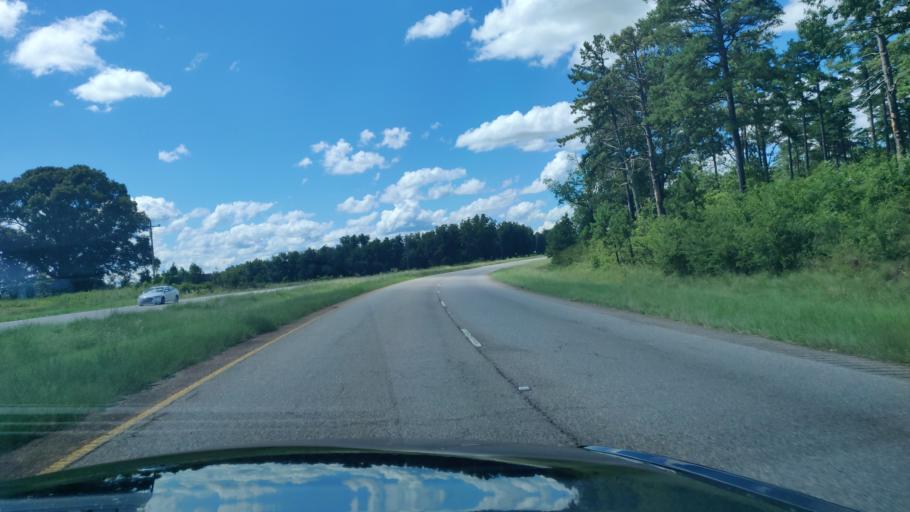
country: US
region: Georgia
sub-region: Stewart County
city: Richland
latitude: 32.0281
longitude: -84.6729
